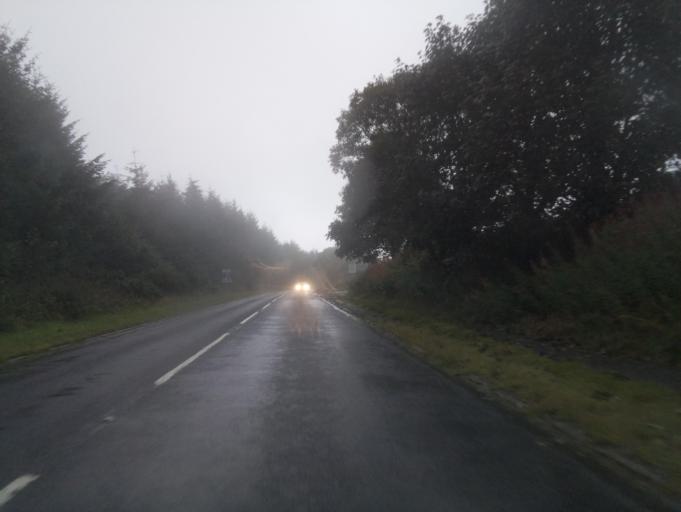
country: GB
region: Scotland
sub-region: Angus
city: Muirhead
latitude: 56.5094
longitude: -3.1677
